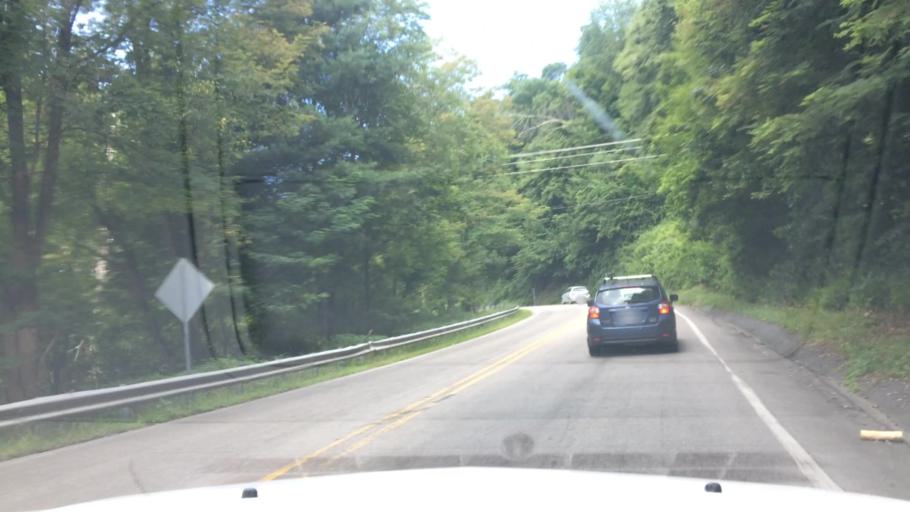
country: US
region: North Carolina
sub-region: Watauga County
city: Boone
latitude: 36.2067
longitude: -81.6314
